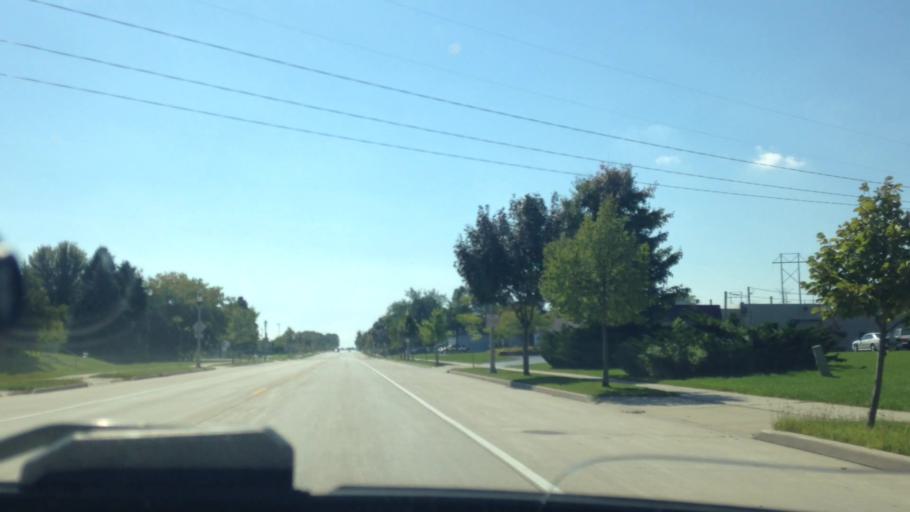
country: US
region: Wisconsin
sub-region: Ozaukee County
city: Port Washington
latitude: 43.3790
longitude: -87.8908
